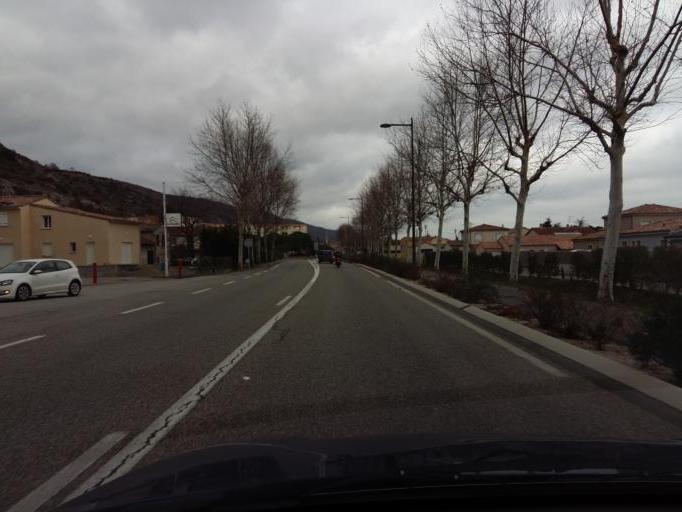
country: FR
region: Rhone-Alpes
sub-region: Departement de l'Ardeche
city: Le Pouzin
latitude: 44.7459
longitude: 4.7452
